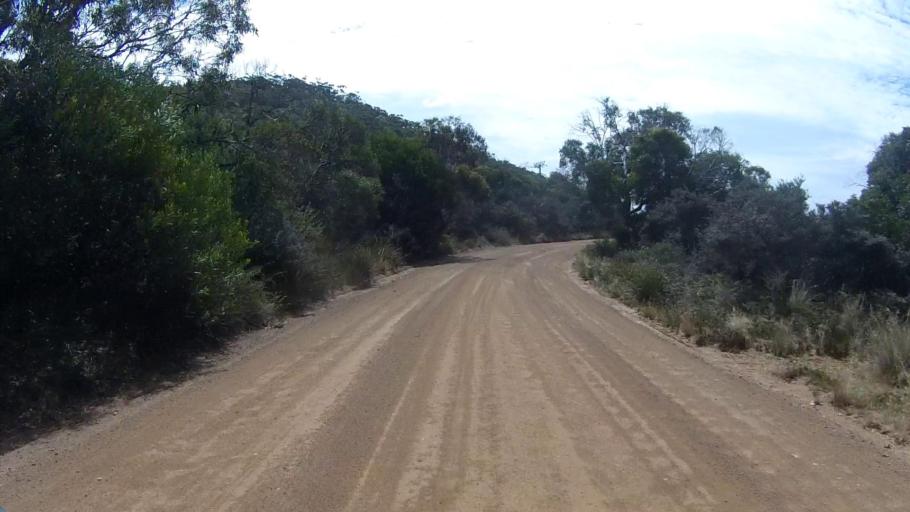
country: AU
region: Tasmania
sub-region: Clarence
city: Sandford
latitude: -43.0250
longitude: 147.4864
